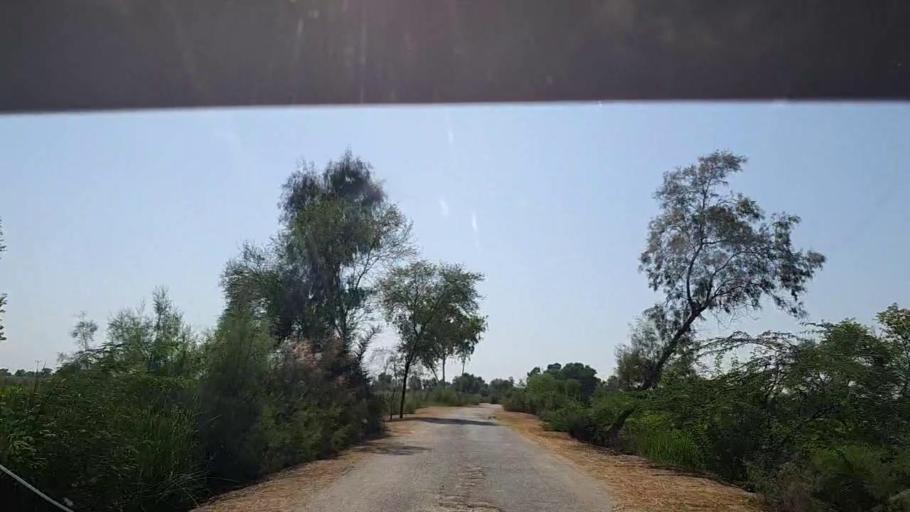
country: PK
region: Sindh
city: Ghauspur
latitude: 28.2190
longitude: 69.0954
